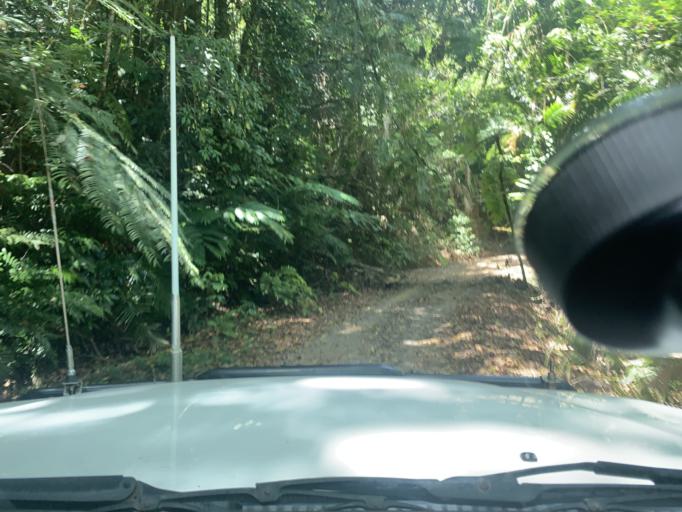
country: AU
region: Queensland
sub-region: Cairns
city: Redlynch
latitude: -16.9668
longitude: 145.6489
